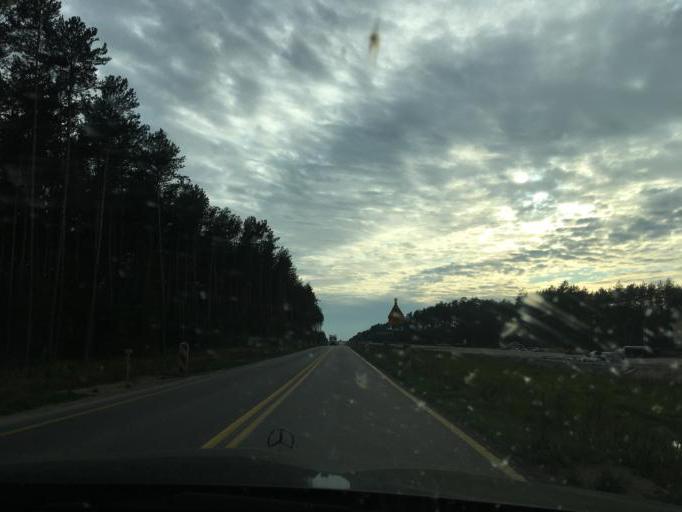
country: PL
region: Masovian Voivodeship
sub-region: Powiat ostrowski
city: Ostrow Mazowiecka
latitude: 52.7756
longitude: 21.8395
